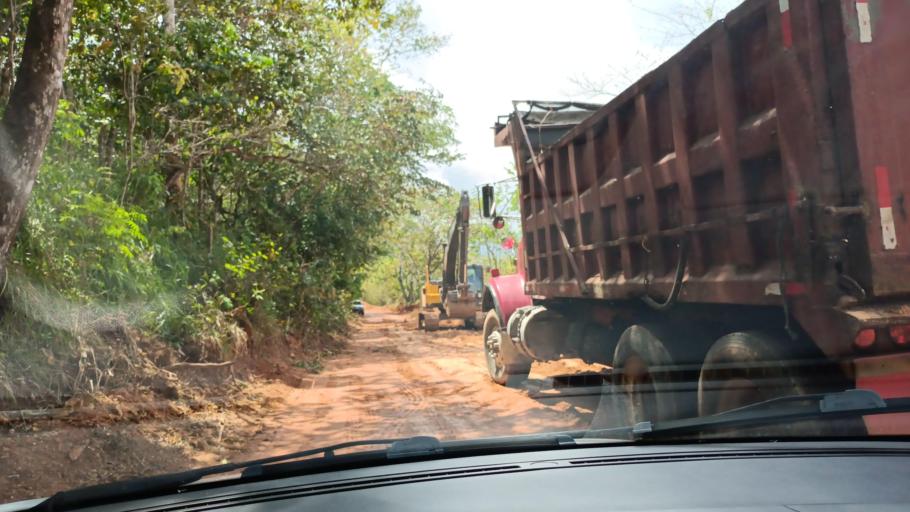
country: PA
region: Panama
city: La Cabima
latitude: 9.1200
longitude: -79.4955
